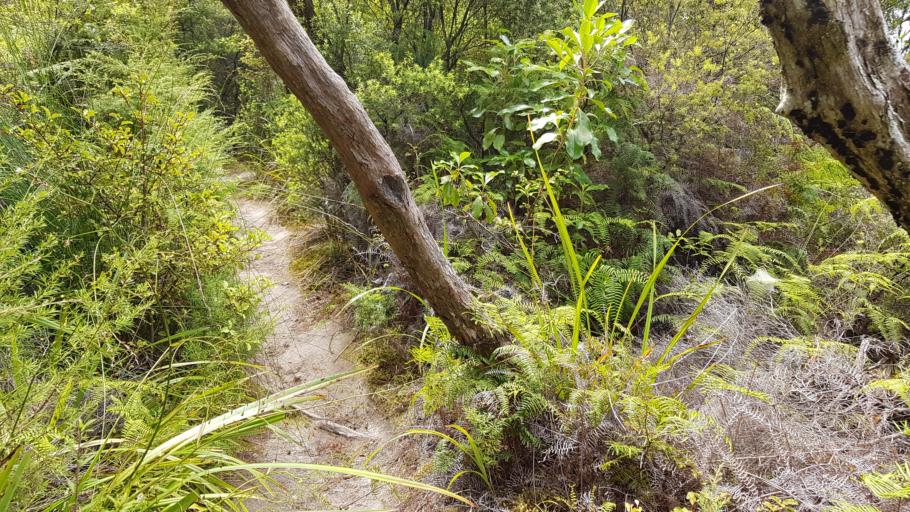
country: NZ
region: Auckland
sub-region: Auckland
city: North Shore
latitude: -36.8245
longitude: 174.7056
